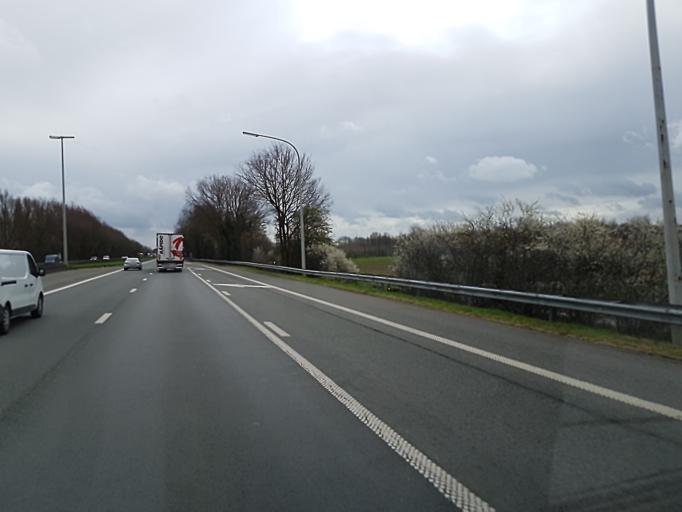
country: BE
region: Wallonia
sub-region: Province du Hainaut
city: Pecq
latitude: 50.6454
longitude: 3.2985
